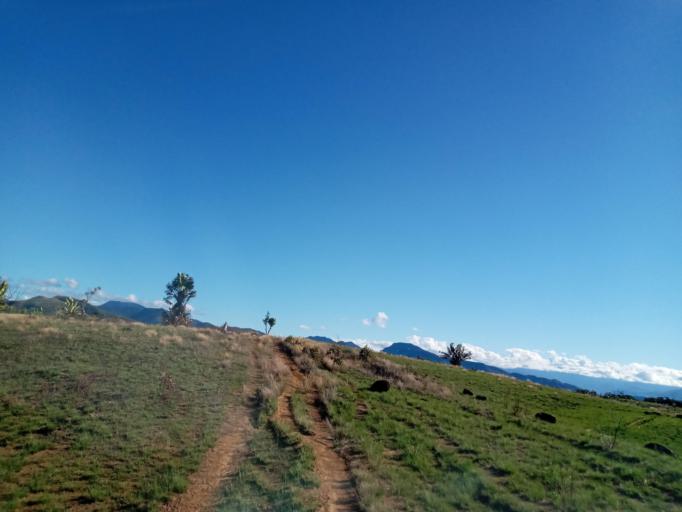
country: MG
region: Anosy
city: Fort Dauphin
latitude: -24.4057
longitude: 47.2497
